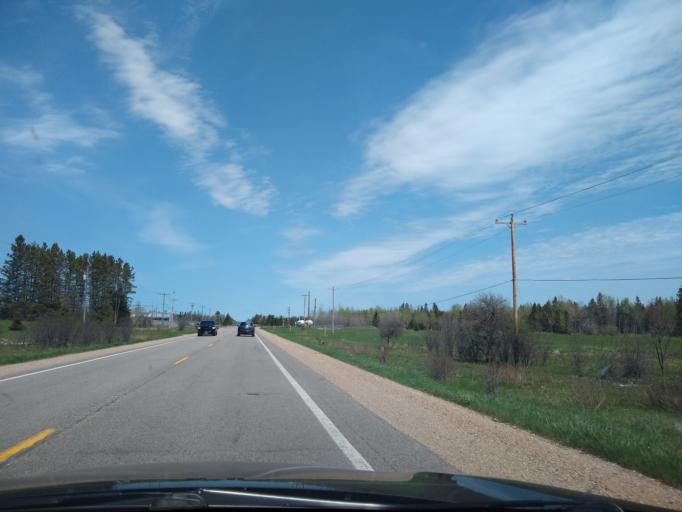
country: US
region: Michigan
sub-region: Delta County
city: Gladstone
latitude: 45.9412
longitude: -86.9720
